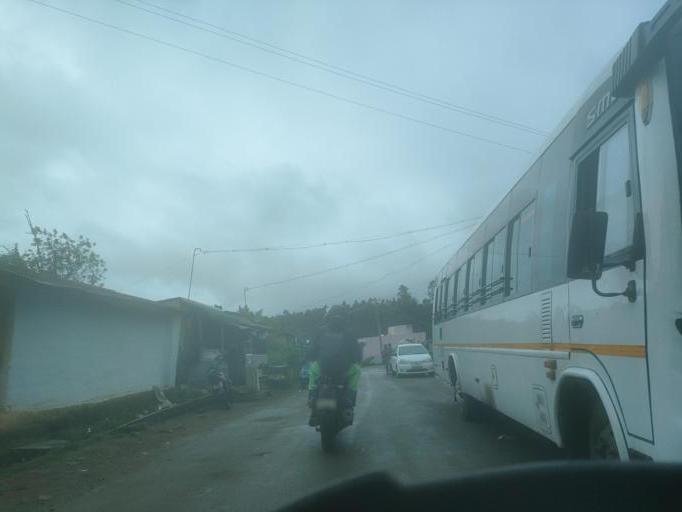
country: IN
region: Tamil Nadu
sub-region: Dindigul
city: Kodaikanal
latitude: 10.2275
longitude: 77.3518
